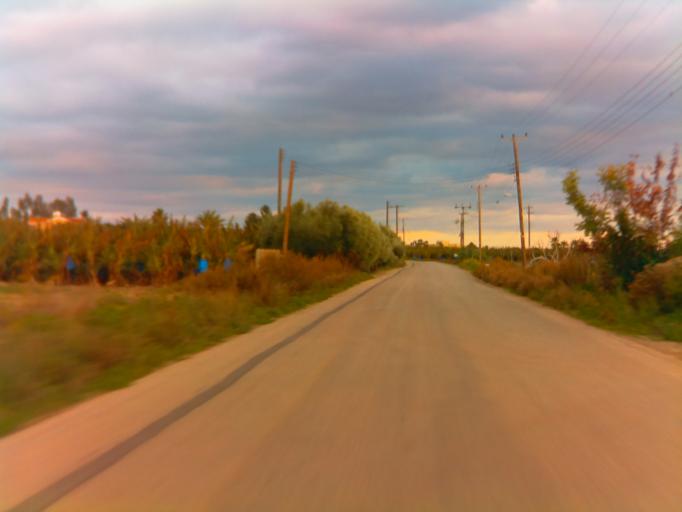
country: CY
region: Pafos
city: Pegeia
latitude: 34.8679
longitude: 32.3502
